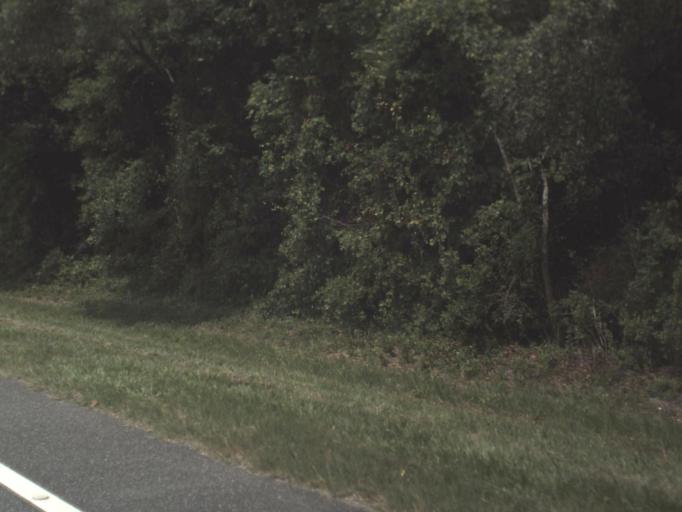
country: US
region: Florida
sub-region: Suwannee County
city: Wellborn
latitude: 30.0675
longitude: -82.9437
